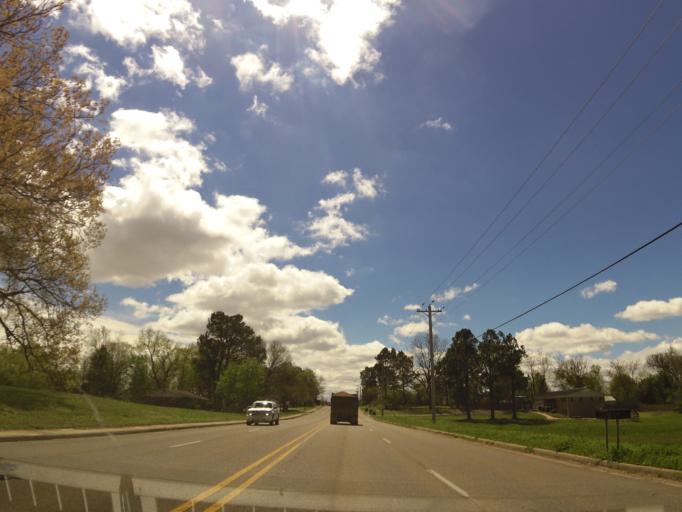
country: US
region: Arkansas
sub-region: Craighead County
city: Jonesboro
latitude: 35.8706
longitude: -90.7029
